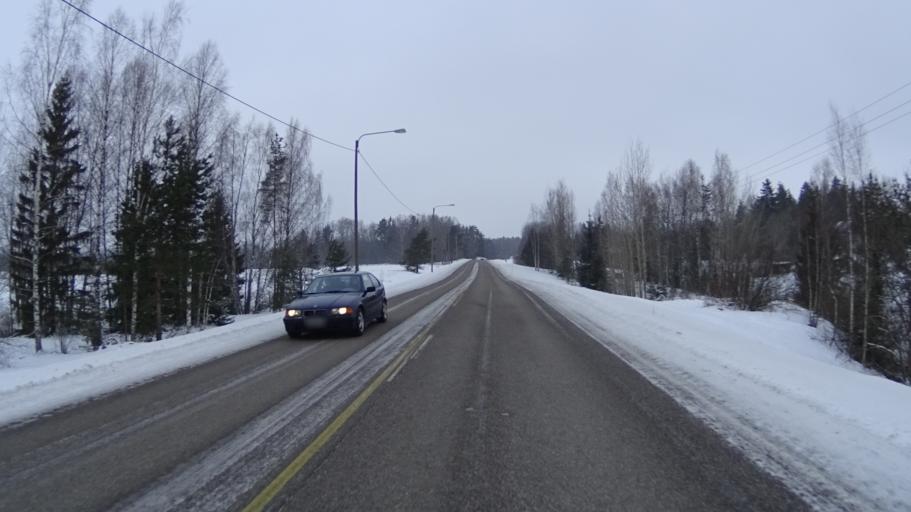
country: FI
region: Uusimaa
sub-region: Helsinki
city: Vihti
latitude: 60.3532
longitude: 24.1841
